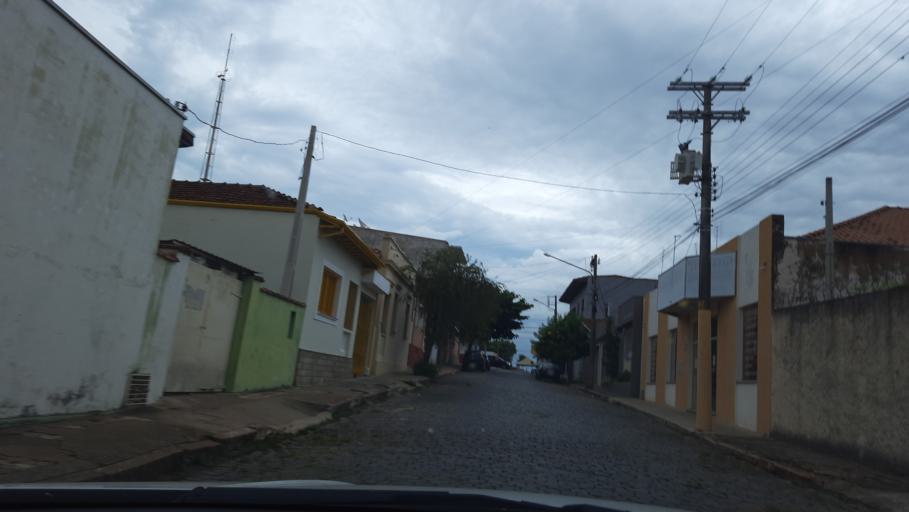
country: BR
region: Sao Paulo
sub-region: Casa Branca
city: Casa Branca
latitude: -21.7754
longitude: -47.0815
